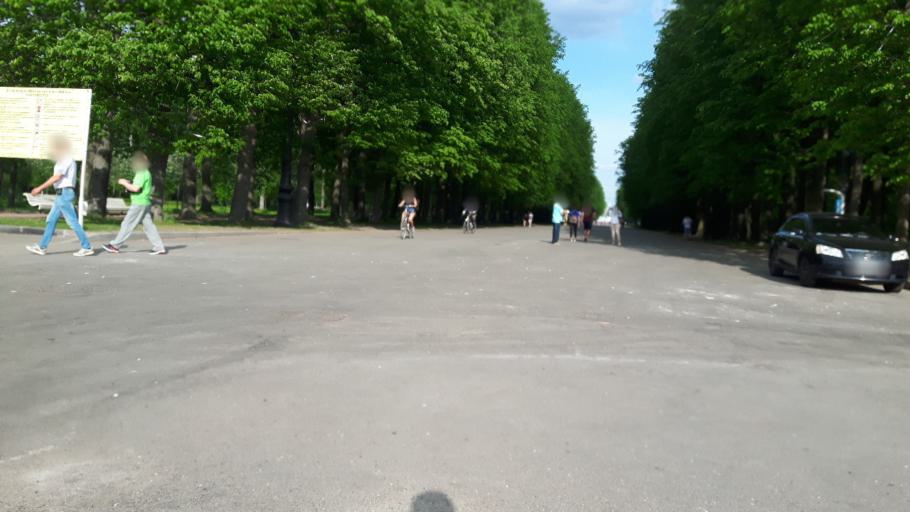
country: RU
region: St.-Petersburg
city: Staraya Derevnya
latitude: 59.9725
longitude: 30.2306
